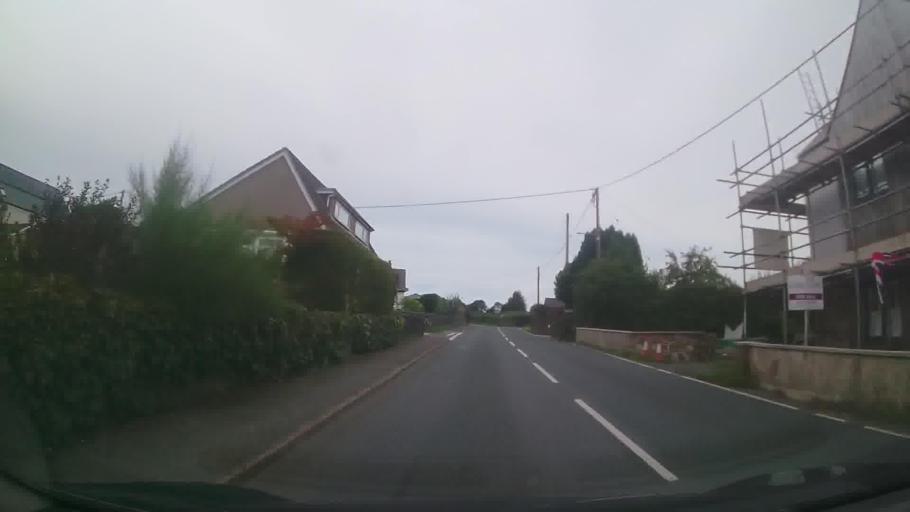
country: GB
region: Wales
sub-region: Pembrokeshire
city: Kilgetty
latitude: 51.7399
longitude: -4.7289
